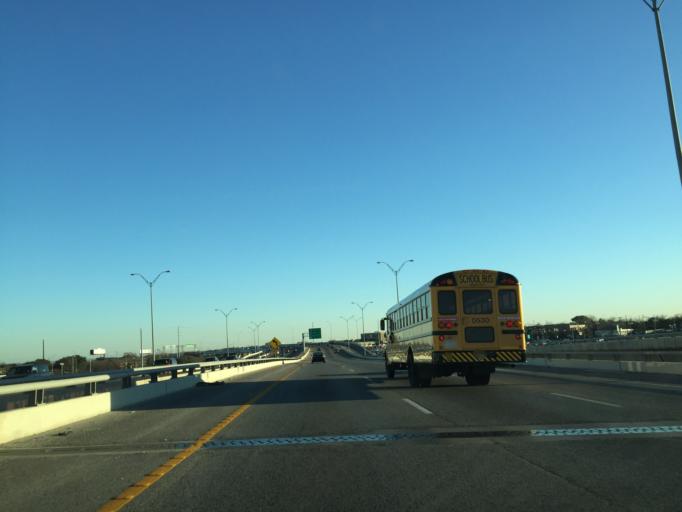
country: US
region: Texas
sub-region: Travis County
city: Austin
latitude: 30.3521
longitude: -97.7143
